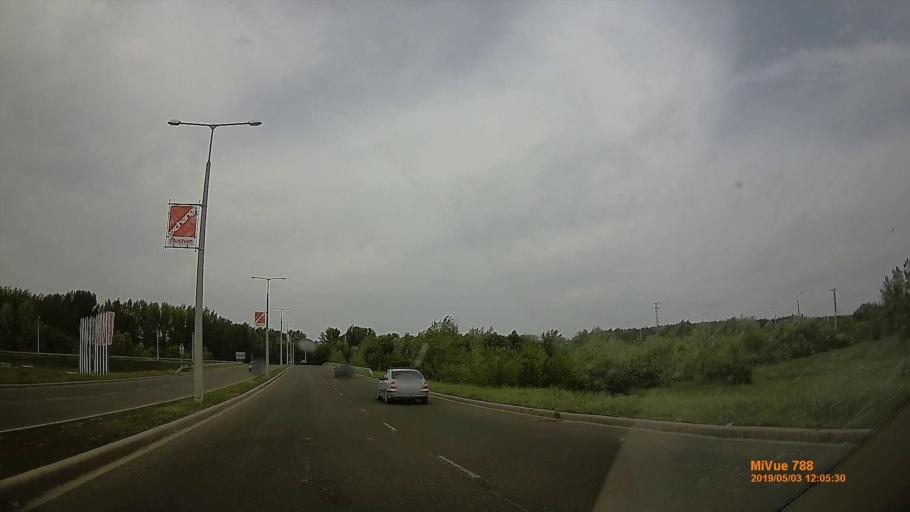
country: HU
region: Jasz-Nagykun-Szolnok
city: Szolnok
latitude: 47.1620
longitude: 20.2010
